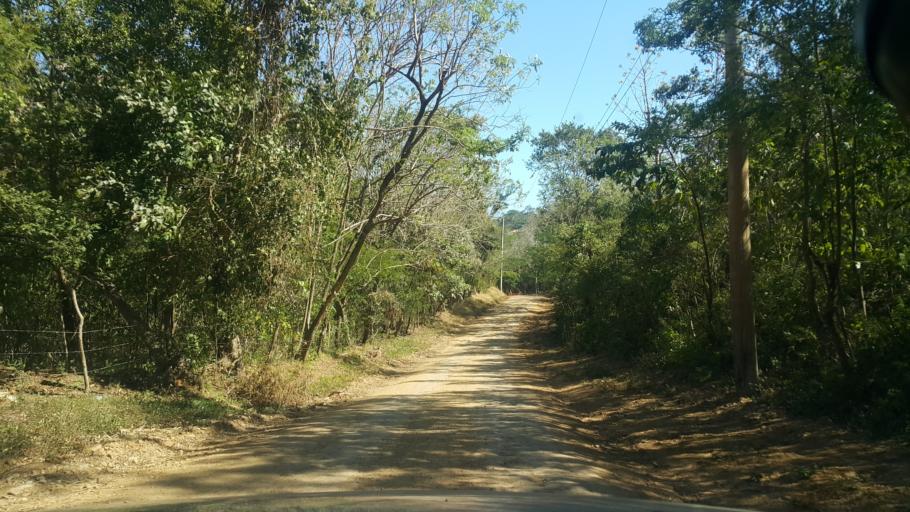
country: NI
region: Rivas
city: San Juan del Sur
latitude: 11.2855
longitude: -85.8750
